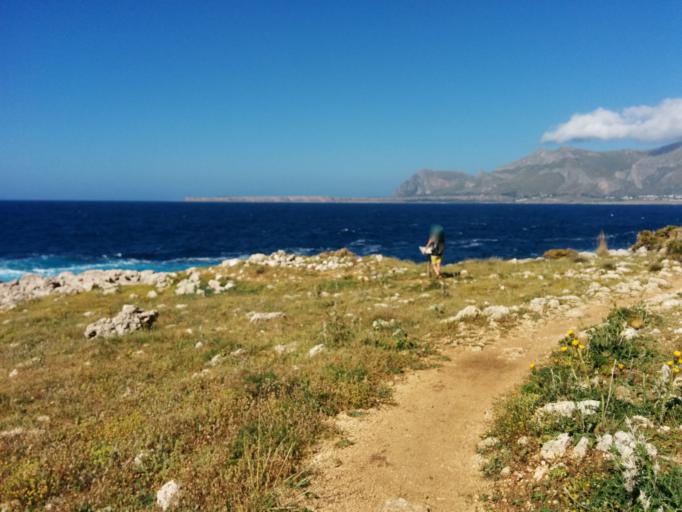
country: IT
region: Sicily
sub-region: Trapani
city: Custonaci
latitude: 38.1139
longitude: 12.6723
